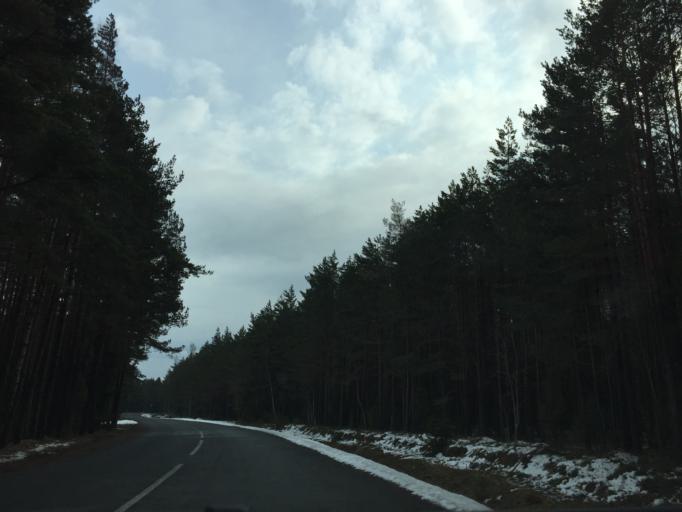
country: EE
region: Saare
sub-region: Kuressaare linn
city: Kuressaare
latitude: 58.4459
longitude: 22.0537
